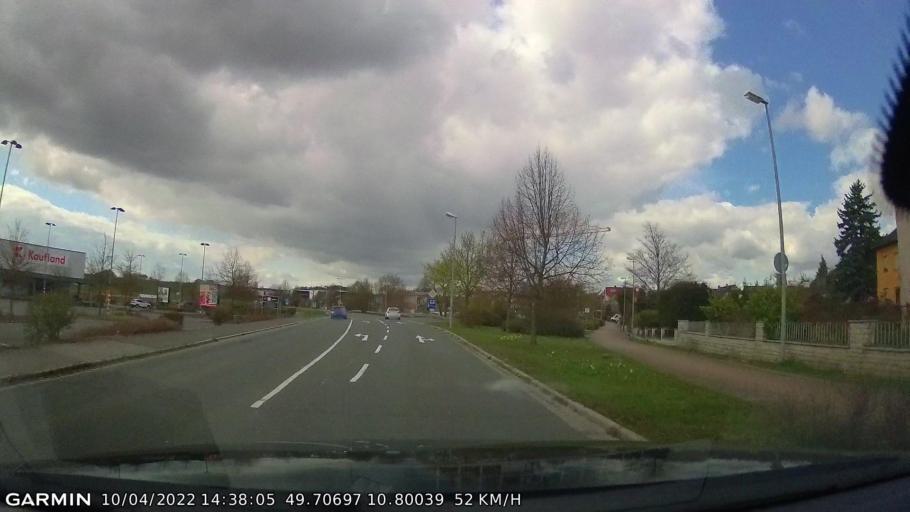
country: DE
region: Bavaria
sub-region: Regierungsbezirk Mittelfranken
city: Hochstadt an der Aisch
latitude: 49.7070
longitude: 10.8003
